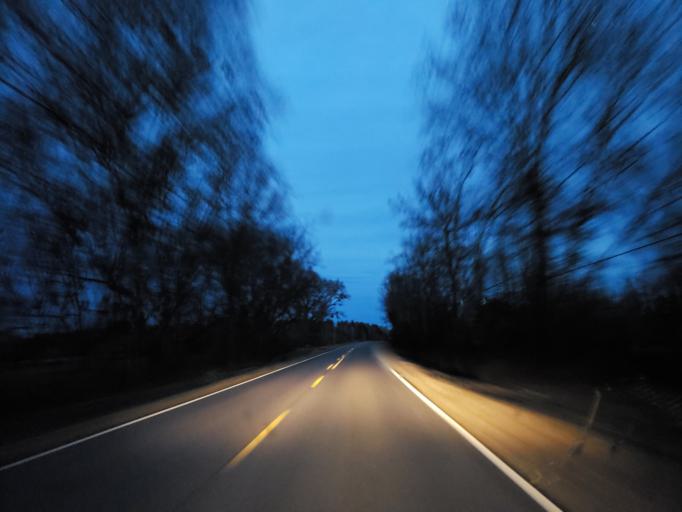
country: US
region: Alabama
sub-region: Greene County
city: Eutaw
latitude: 32.8872
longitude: -87.9432
